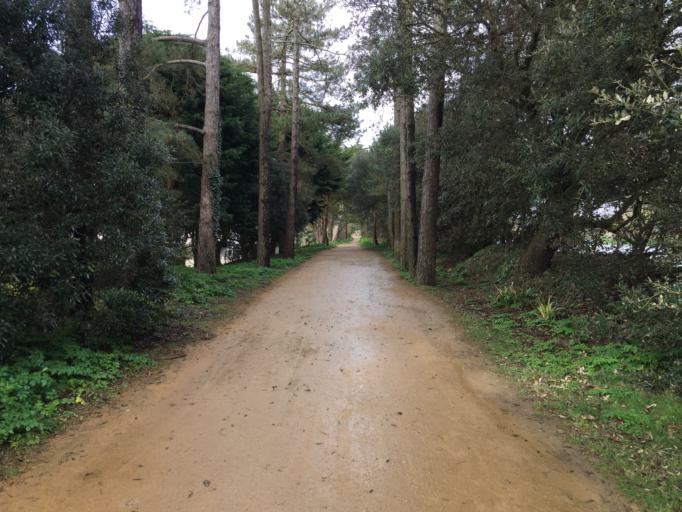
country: JE
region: St Helier
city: Saint Helier
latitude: 49.1842
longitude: -2.2231
